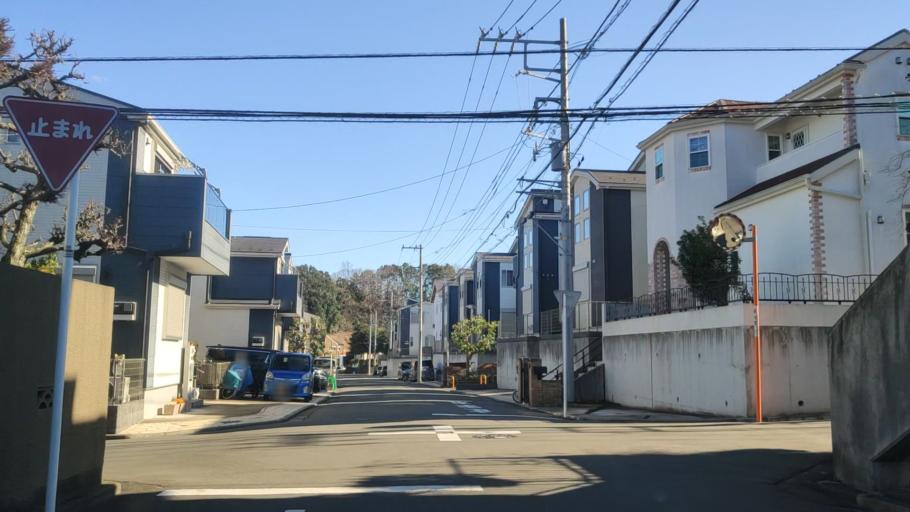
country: JP
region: Kanagawa
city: Minami-rinkan
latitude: 35.5064
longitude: 139.5258
